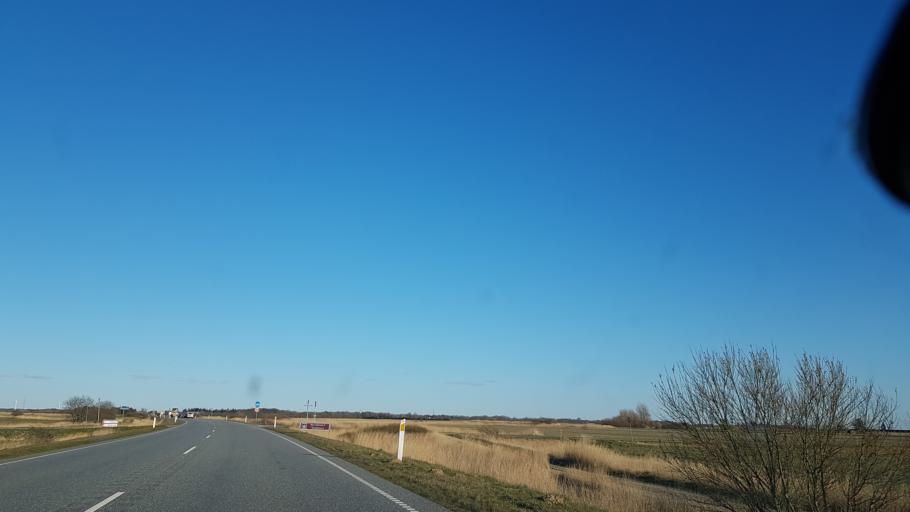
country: DK
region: South Denmark
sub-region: Esbjerg Kommune
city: Tjaereborg
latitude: 55.4409
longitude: 8.6109
